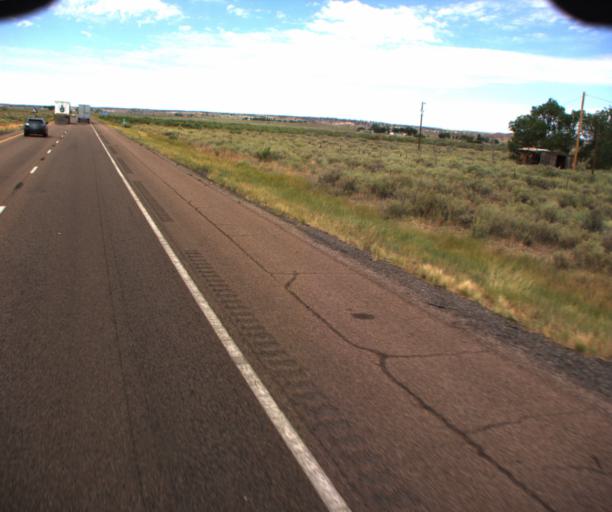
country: US
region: Arizona
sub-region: Apache County
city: Houck
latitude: 35.1966
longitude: -109.4075
